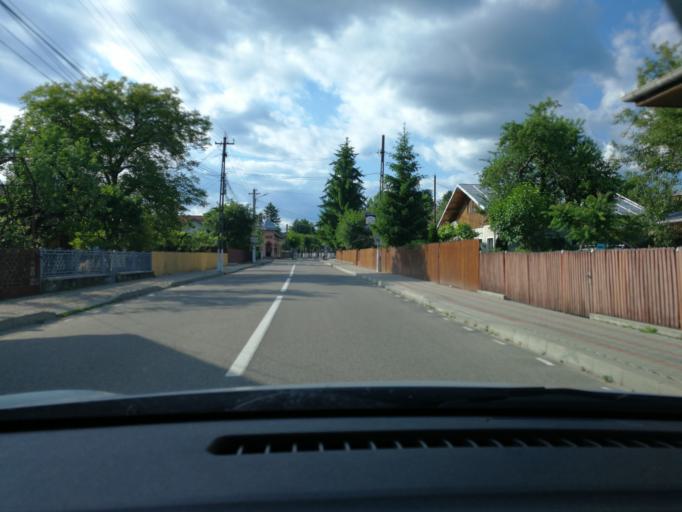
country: RO
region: Prahova
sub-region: Comuna Cornu
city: Cornu de Jos
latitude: 45.1539
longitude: 25.7040
